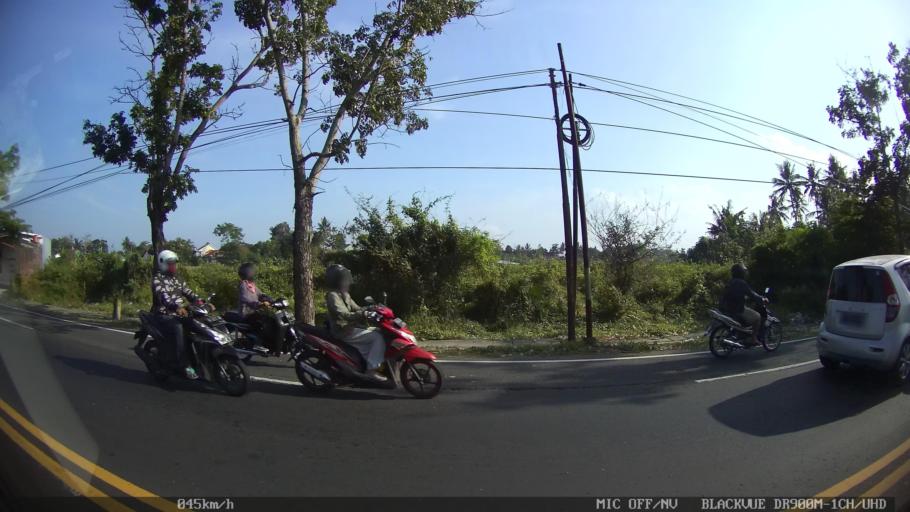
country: ID
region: Daerah Istimewa Yogyakarta
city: Gamping Lor
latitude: -7.8020
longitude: 110.3157
